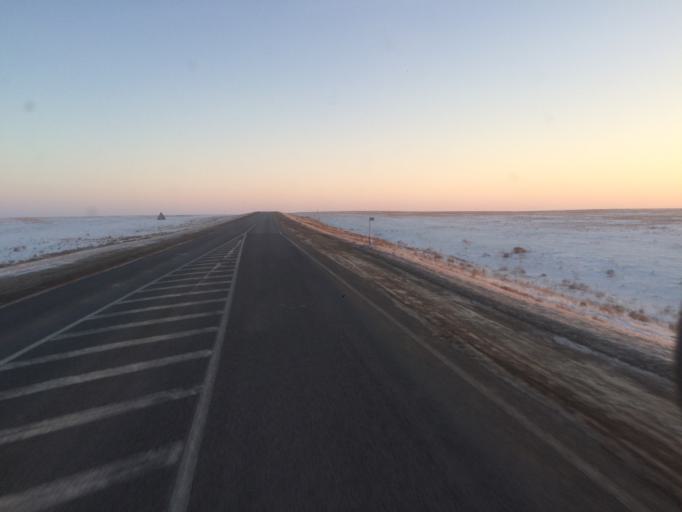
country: KZ
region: Qyzylorda
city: Sekseuil
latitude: 47.5725
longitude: 61.5111
